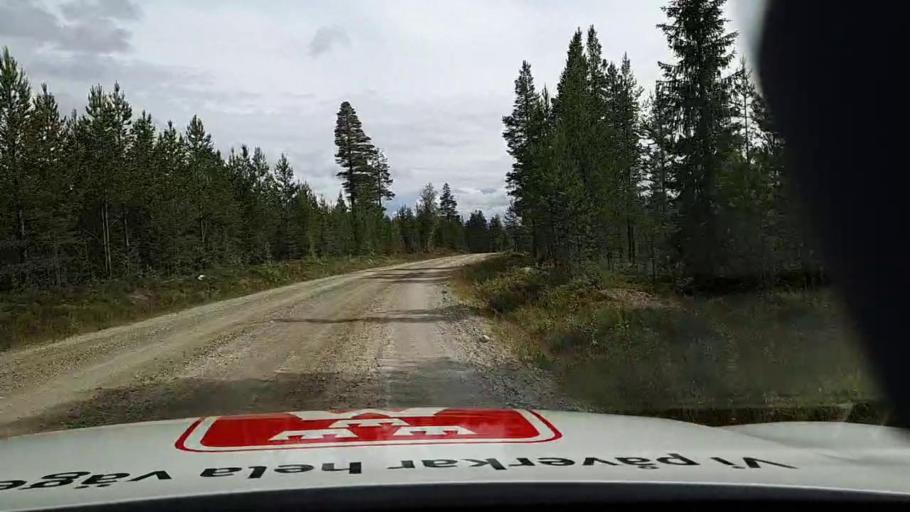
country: SE
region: Jaemtland
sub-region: Are Kommun
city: Jarpen
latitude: 62.5331
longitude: 13.4820
